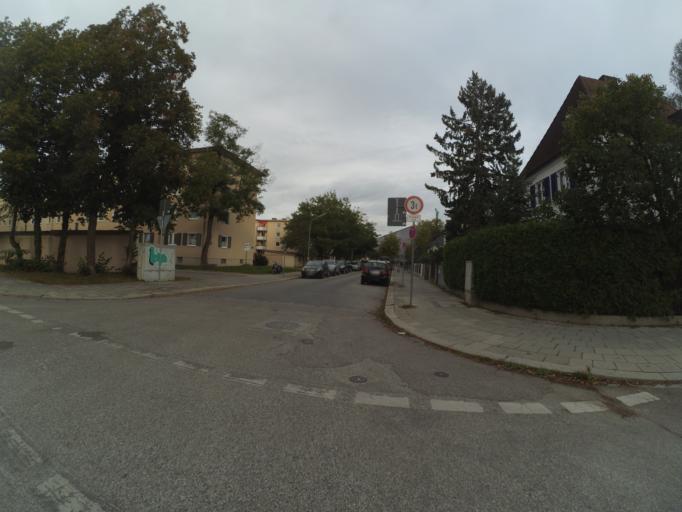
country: DE
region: Bavaria
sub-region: Upper Bavaria
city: Karlsfeld
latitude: 48.1756
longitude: 11.5127
